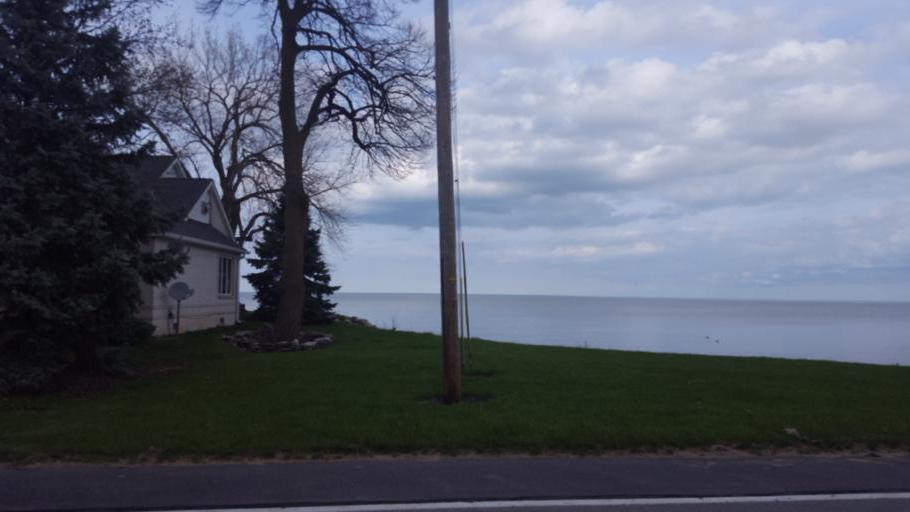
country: US
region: Ohio
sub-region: Erie County
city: Sandusky
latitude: 41.5339
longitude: -82.7140
